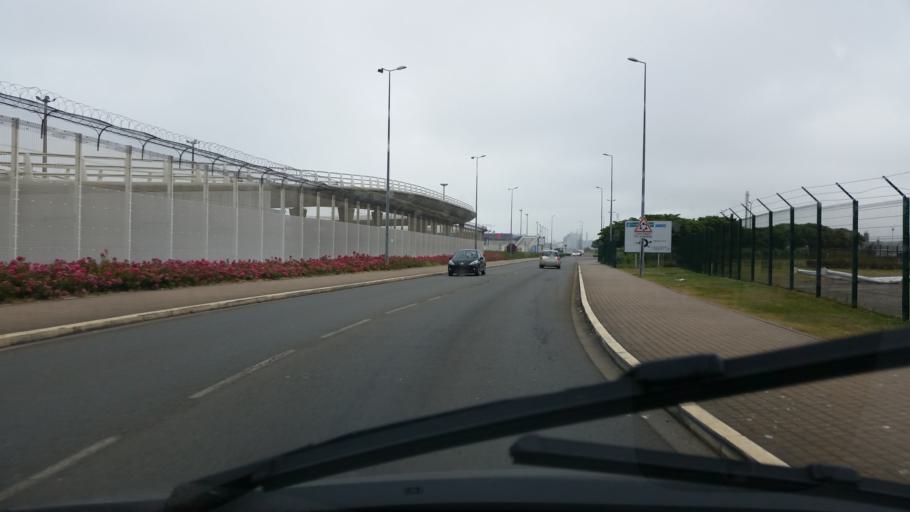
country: FR
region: Nord-Pas-de-Calais
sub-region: Departement du Pas-de-Calais
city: Calais
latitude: 50.9643
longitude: 1.8586
